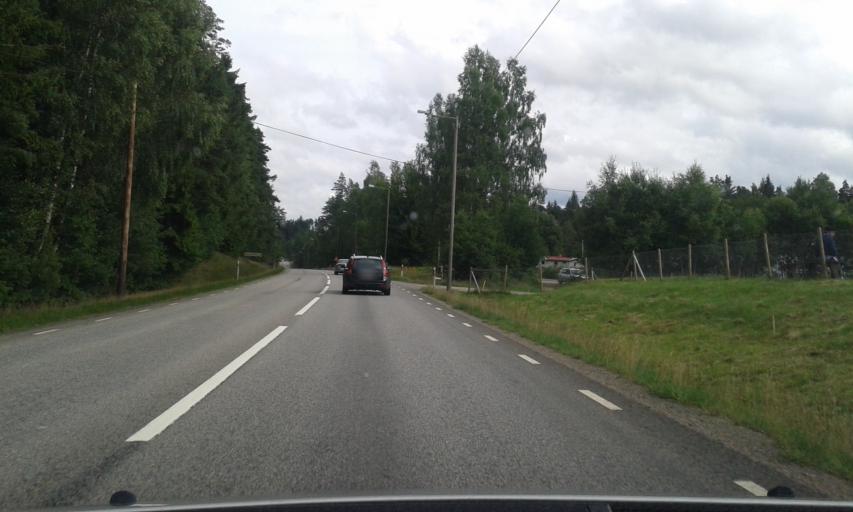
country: SE
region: Vaestra Goetaland
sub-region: Marks Kommun
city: Horred
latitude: 57.1441
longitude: 12.6915
